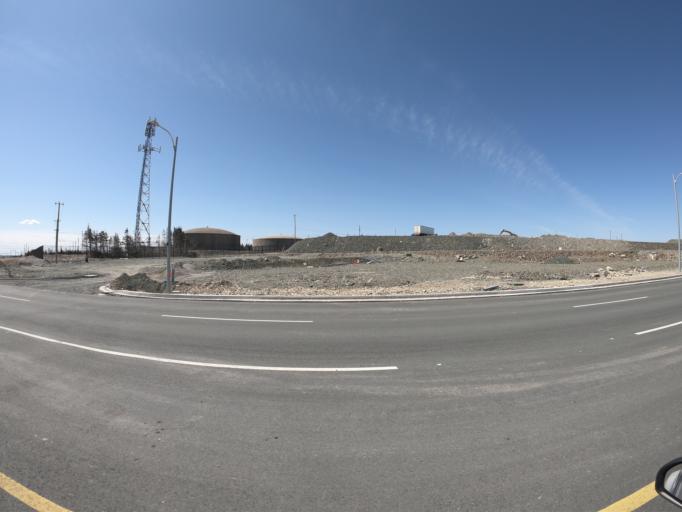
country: CA
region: Newfoundland and Labrador
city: Mount Pearl
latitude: 47.5082
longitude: -52.8301
